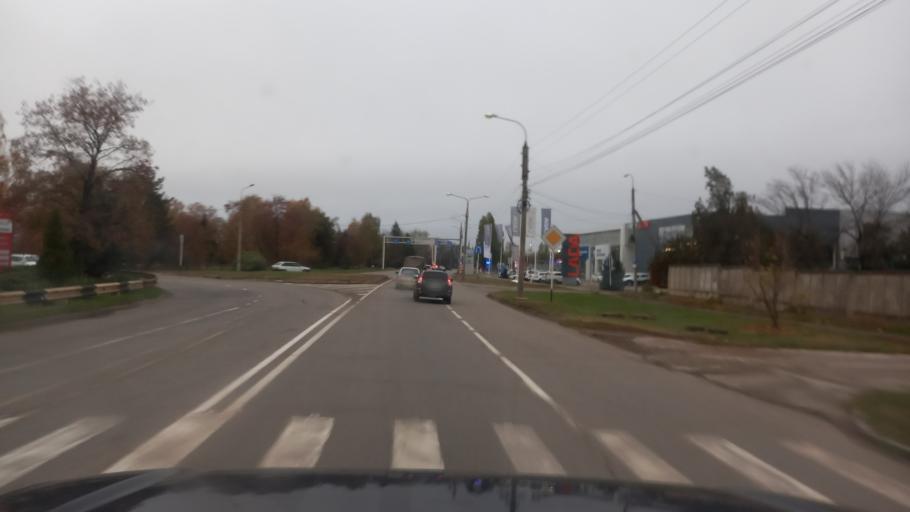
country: RU
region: Adygeya
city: Maykop
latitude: 44.6228
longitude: 40.0588
